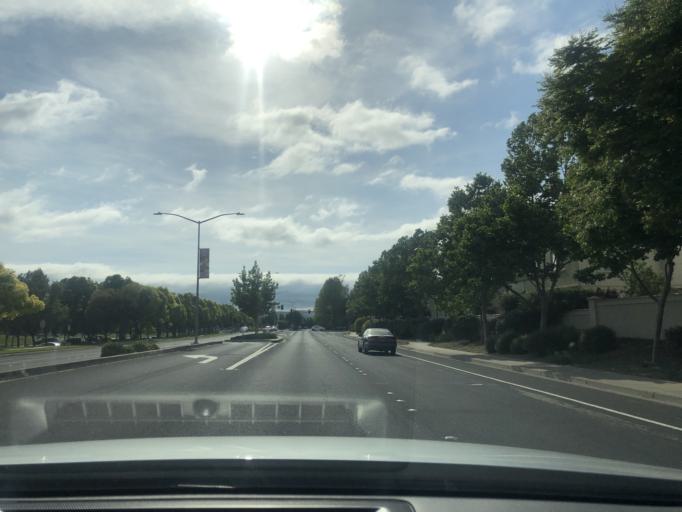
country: US
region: California
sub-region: Alameda County
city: Pleasanton
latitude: 37.7127
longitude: -121.8746
